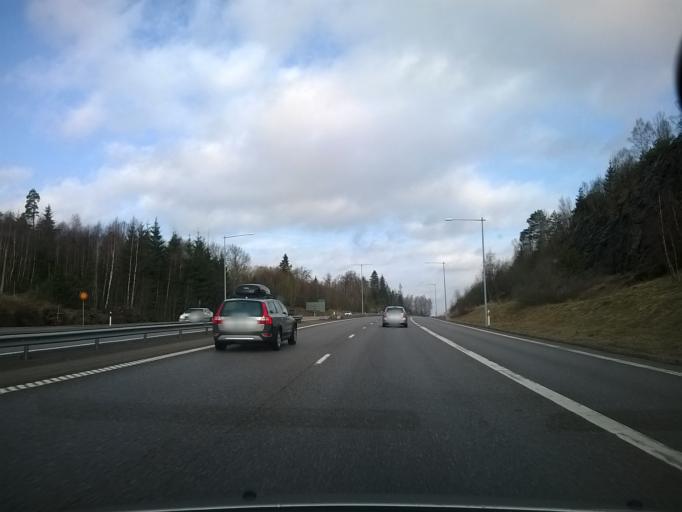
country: SE
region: Vaestra Goetaland
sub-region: Uddevalla Kommun
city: Ljungskile
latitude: 58.2933
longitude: 11.8661
